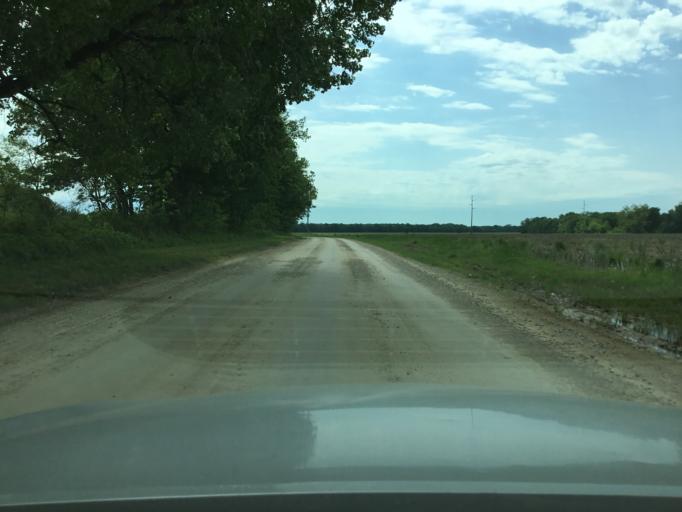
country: US
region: Kansas
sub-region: Montgomery County
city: Coffeyville
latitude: 37.0060
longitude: -95.6037
